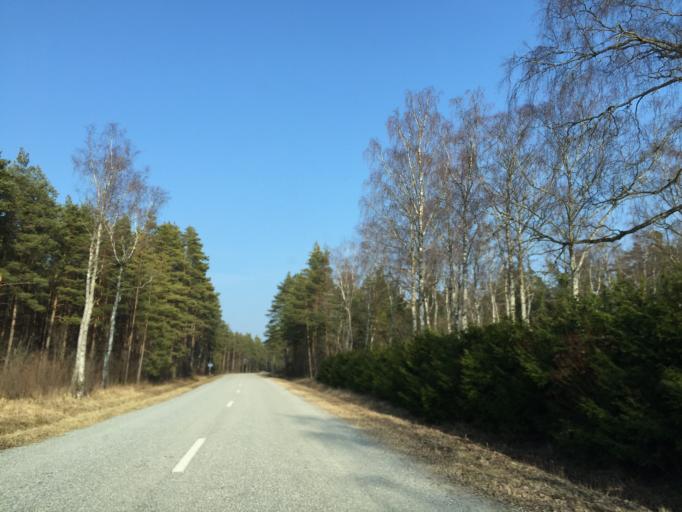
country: EE
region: Saare
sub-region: Orissaare vald
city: Orissaare
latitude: 58.5614
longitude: 23.3359
